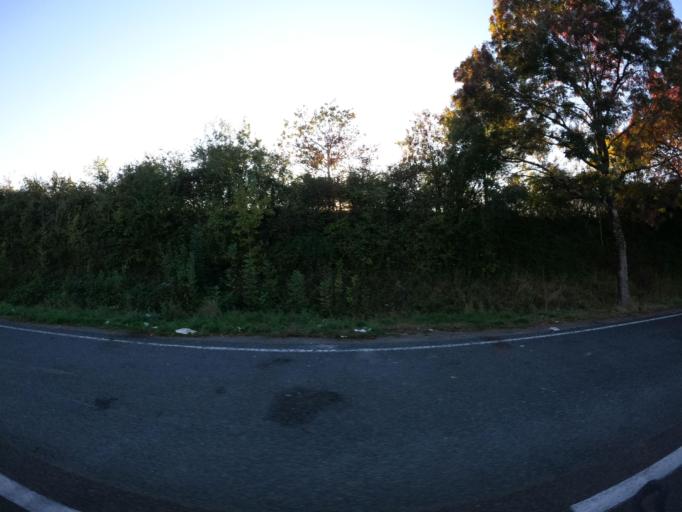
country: FR
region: Pays de la Loire
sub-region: Departement de la Vendee
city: Sainte-Hermine
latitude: 46.5585
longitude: -1.0457
